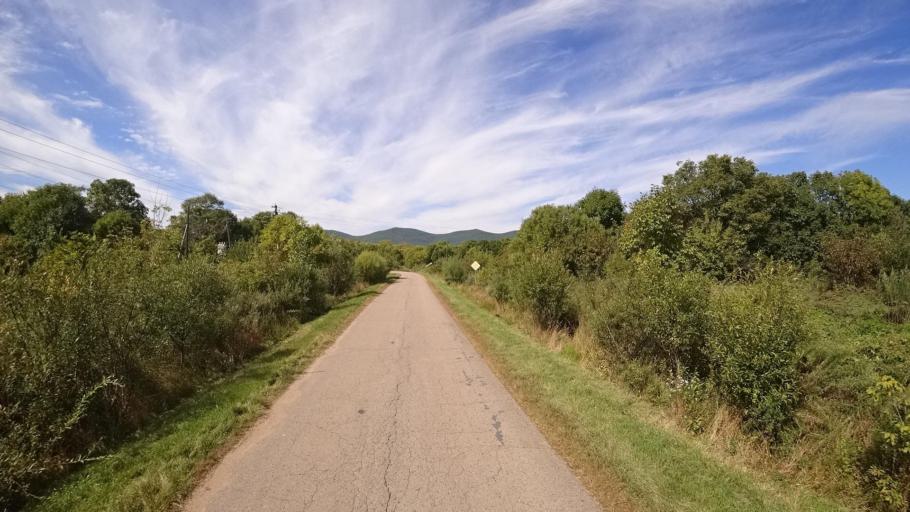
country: RU
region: Primorskiy
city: Kirovskiy
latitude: 44.7593
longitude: 133.6090
